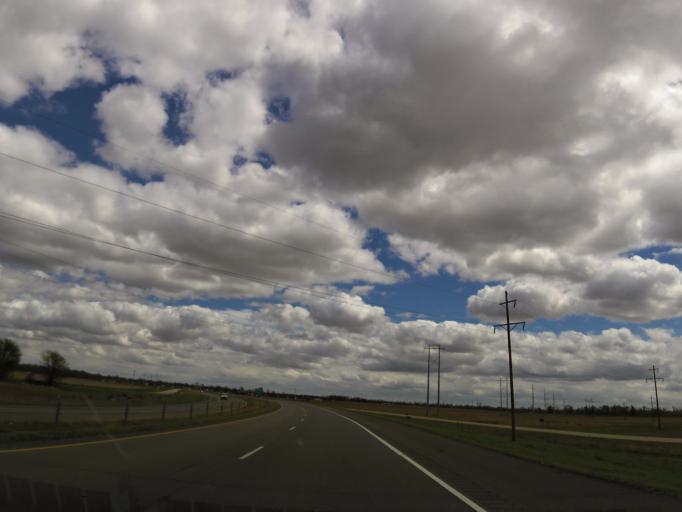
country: US
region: Arkansas
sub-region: Poinsett County
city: Marked Tree
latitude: 35.5283
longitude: -90.4543
